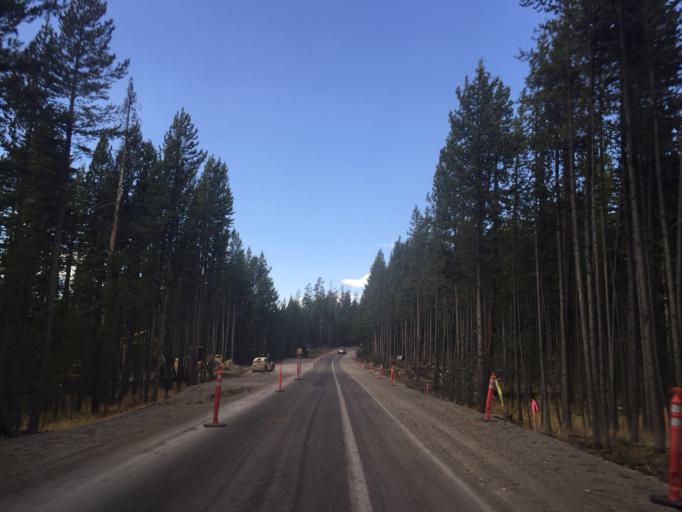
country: US
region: Montana
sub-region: Gallatin County
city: West Yellowstone
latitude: 44.7339
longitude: -110.4850
